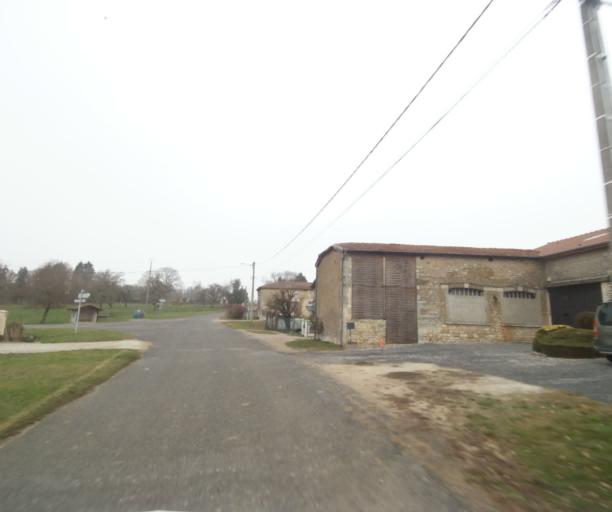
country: FR
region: Champagne-Ardenne
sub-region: Departement de la Haute-Marne
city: Bienville
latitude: 48.5053
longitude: 5.0365
